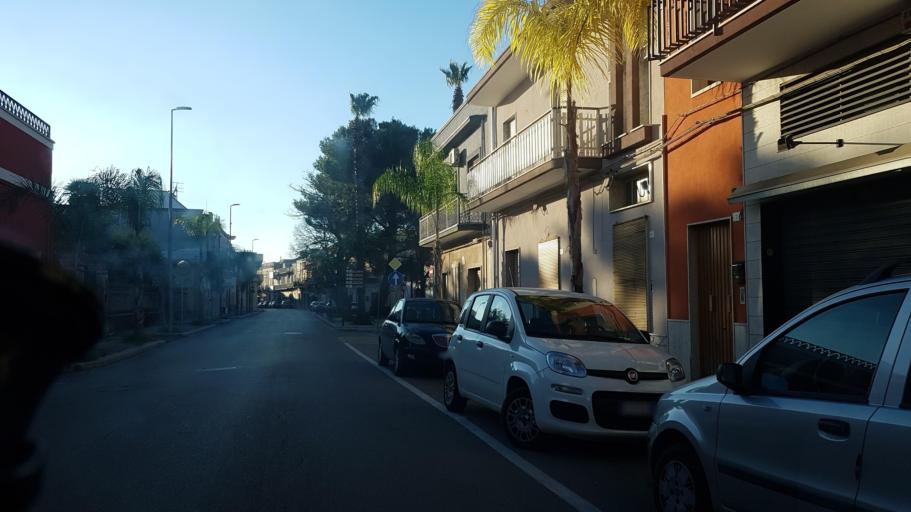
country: IT
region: Apulia
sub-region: Provincia di Brindisi
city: Latiano
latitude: 40.5529
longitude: 17.7225
